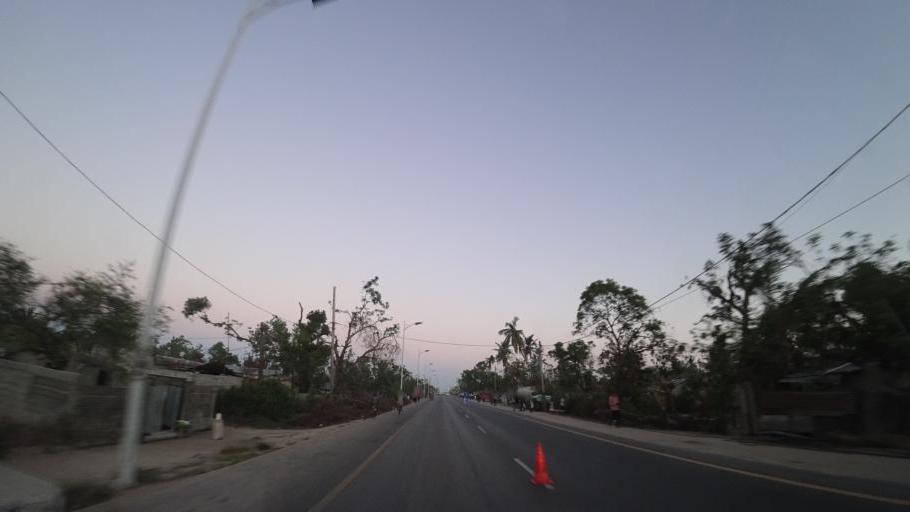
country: MZ
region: Sofala
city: Dondo
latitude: -19.5348
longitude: 34.6319
